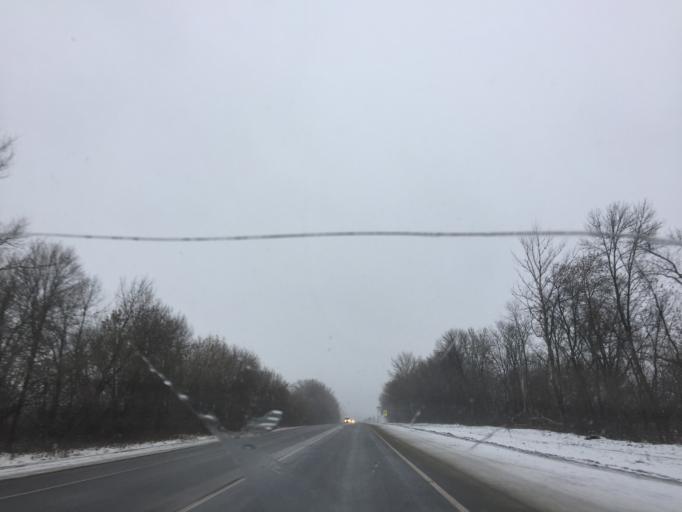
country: RU
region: Tula
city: Plavsk
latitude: 53.7305
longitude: 37.3068
